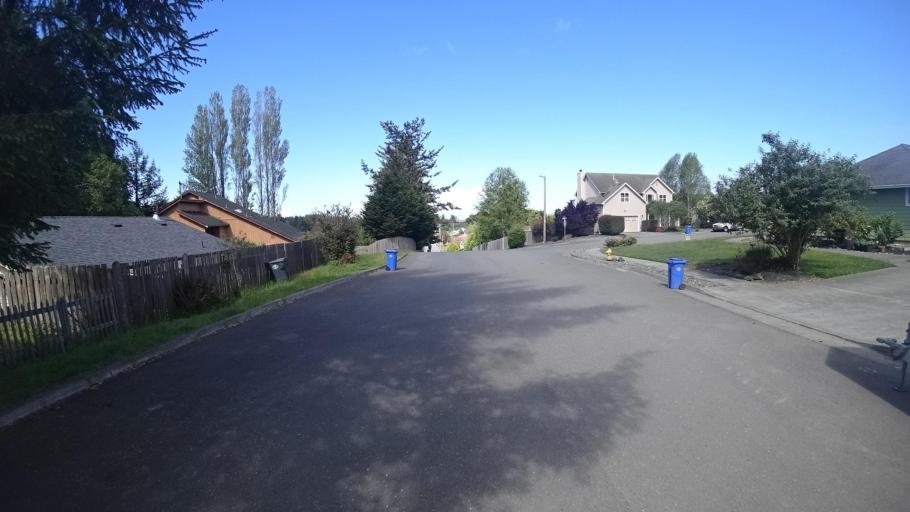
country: US
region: California
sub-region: Humboldt County
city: McKinleyville
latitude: 40.9342
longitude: -124.0794
